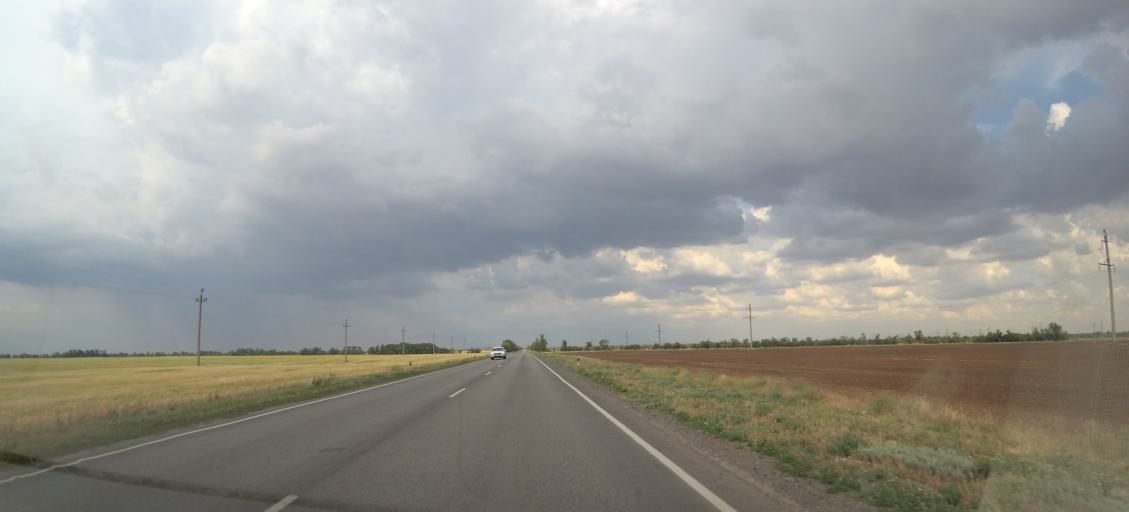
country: RU
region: Rostov
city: Zimovniki
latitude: 47.1238
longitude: 42.3995
